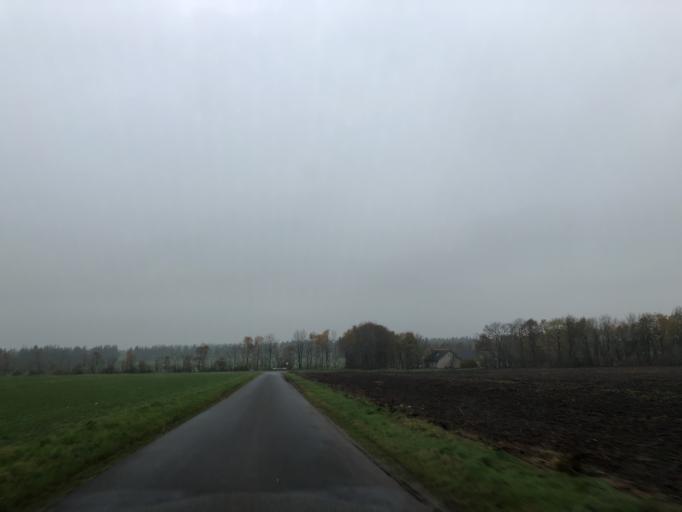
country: DK
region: Central Jutland
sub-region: Ringkobing-Skjern Kommune
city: Videbaek
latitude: 56.1962
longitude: 8.6439
